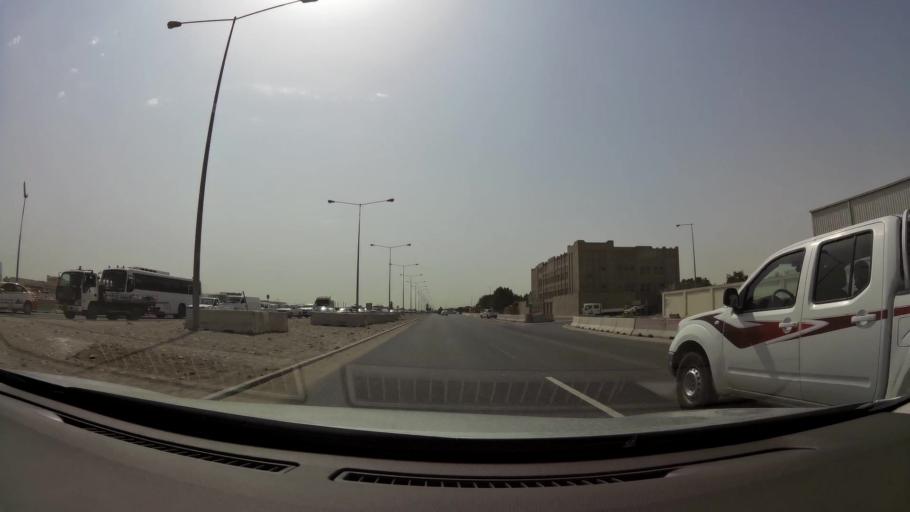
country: QA
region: Al Wakrah
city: Al Wukayr
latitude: 25.1884
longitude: 51.4580
